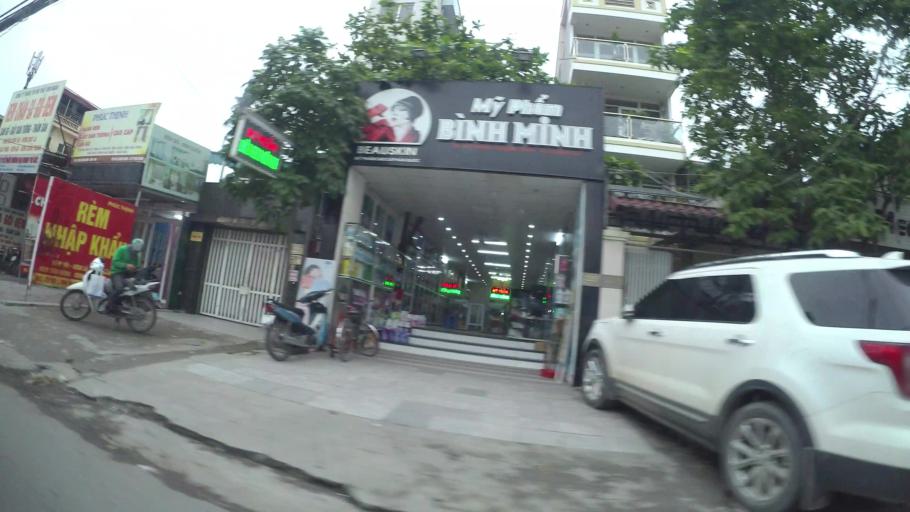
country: VN
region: Ha Noi
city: Hai BaTrung
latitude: 20.9847
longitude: 105.8728
